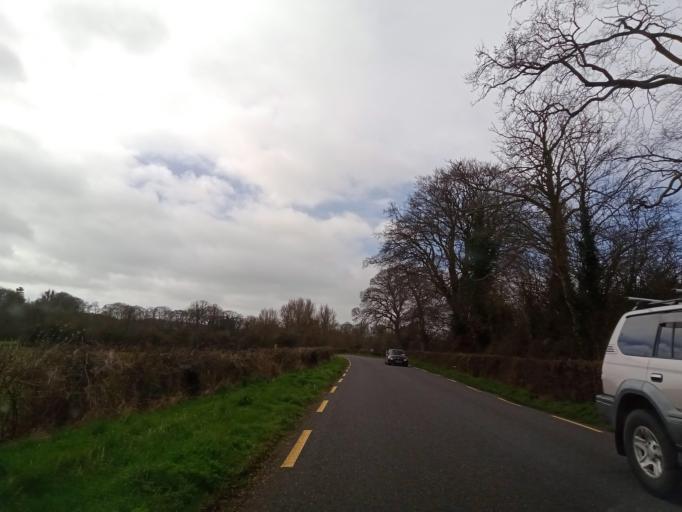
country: IE
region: Leinster
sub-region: Kilkenny
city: Ballyragget
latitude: 52.7161
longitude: -7.3205
